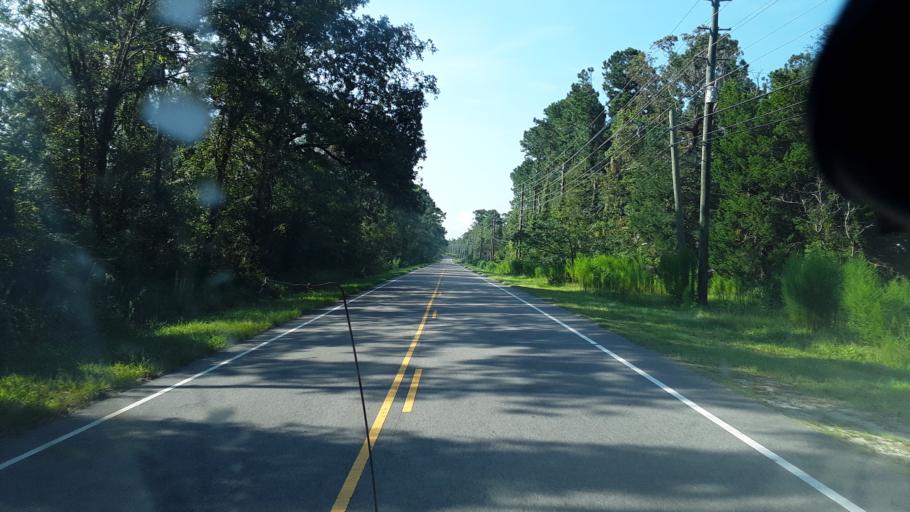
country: US
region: North Carolina
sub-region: Brunswick County
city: Belville
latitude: 34.1786
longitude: -77.9905
